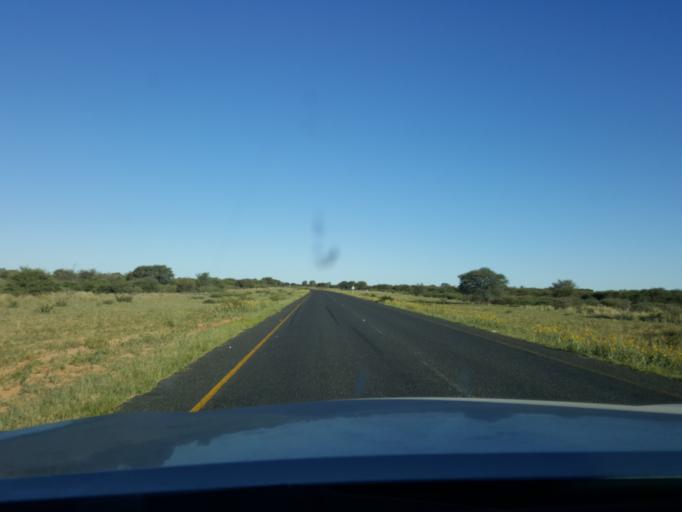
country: BW
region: Southern
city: Khakhea
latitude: -24.2166
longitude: 23.2277
